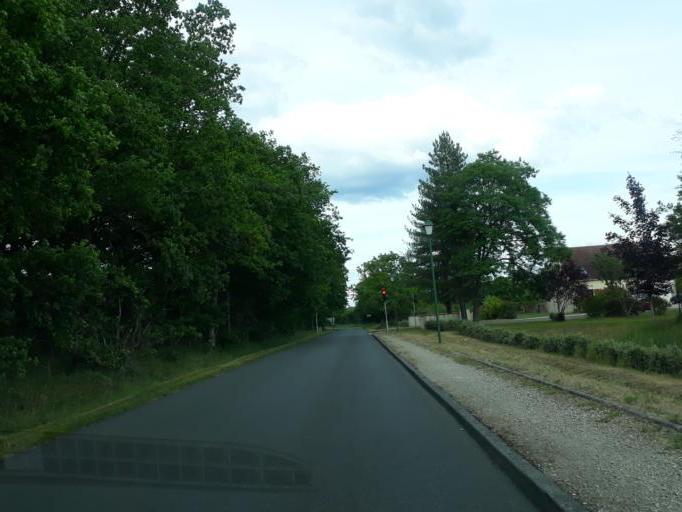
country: FR
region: Centre
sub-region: Departement du Loiret
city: La Ferte-Saint-Aubin
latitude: 47.7243
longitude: 1.9588
